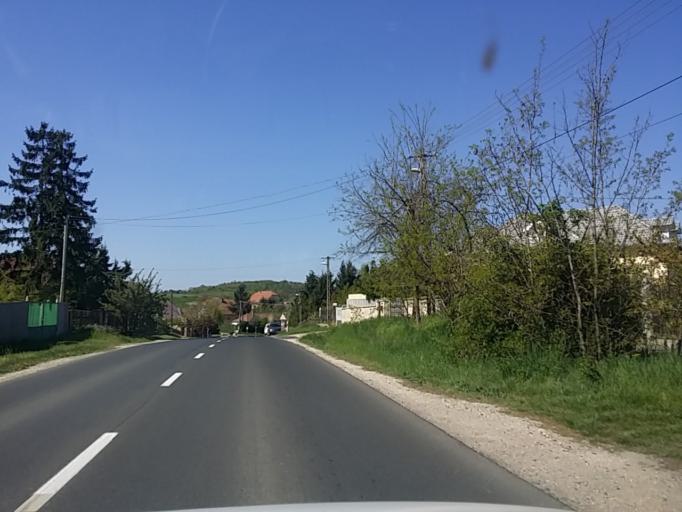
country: HU
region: Pest
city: Mogyorod
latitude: 47.5952
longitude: 19.2752
